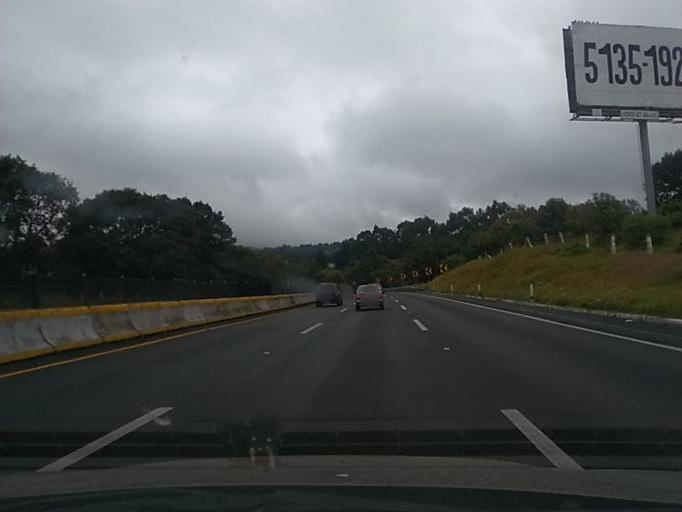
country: MX
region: Mexico City
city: Xochimilco
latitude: 19.1944
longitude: -99.1561
